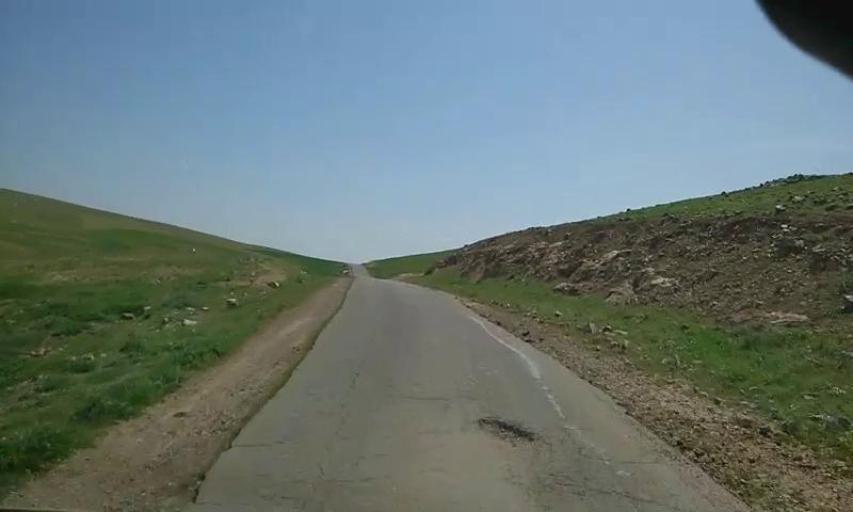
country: PS
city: `Arab ar Rashaydah
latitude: 31.5523
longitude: 35.2510
